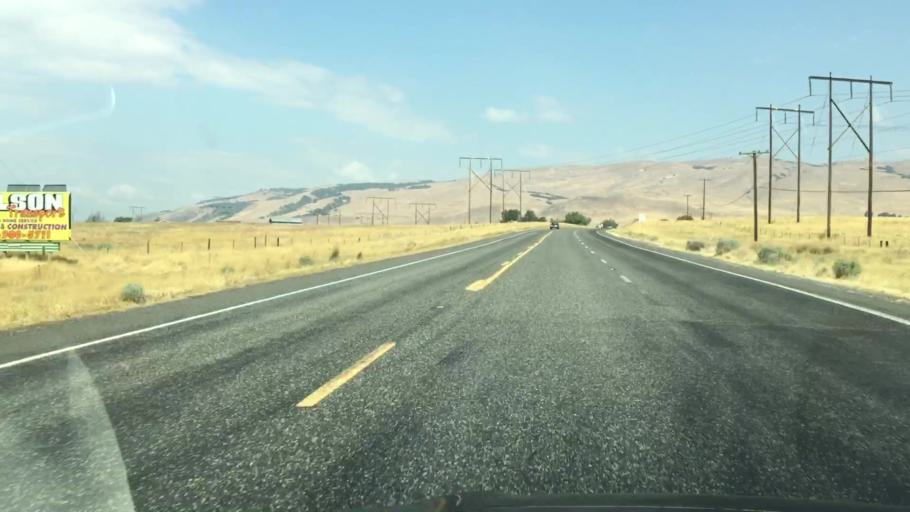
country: US
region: Washington
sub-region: Klickitat County
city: Dallesport
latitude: 45.6326
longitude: -121.1521
